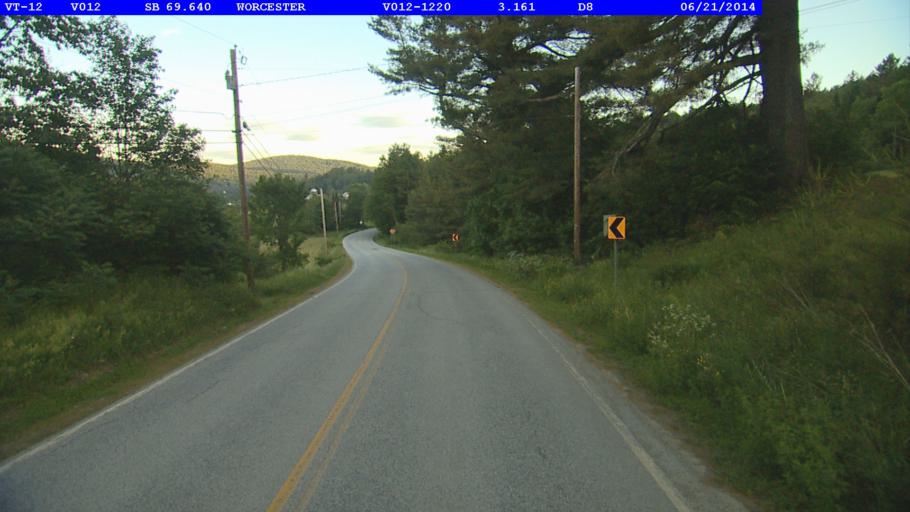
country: US
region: Vermont
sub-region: Washington County
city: Montpelier
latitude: 44.3929
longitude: -72.5570
